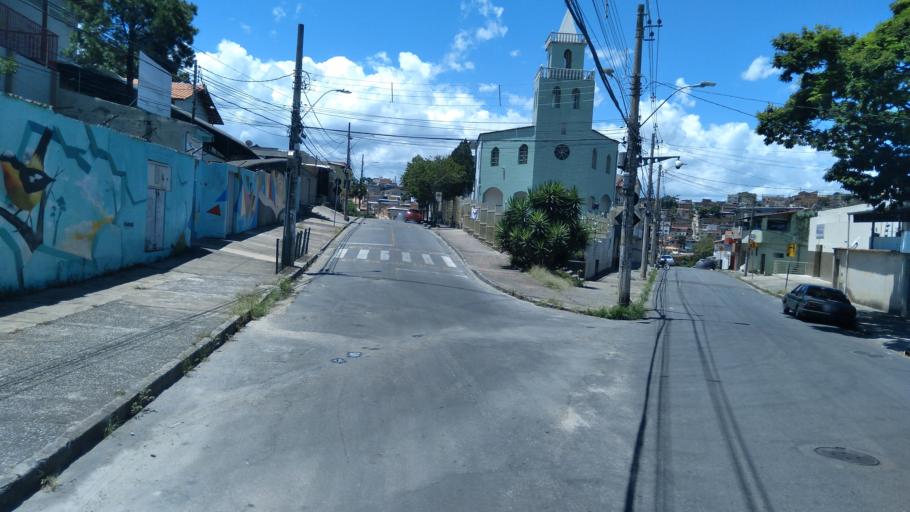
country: BR
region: Minas Gerais
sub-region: Santa Luzia
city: Santa Luzia
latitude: -19.8350
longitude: -43.8904
